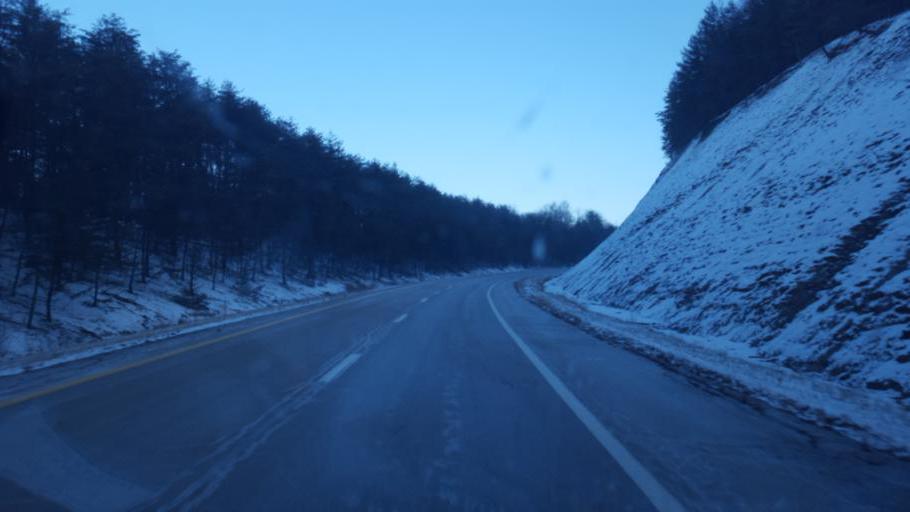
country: US
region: Ohio
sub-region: Adams County
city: Peebles
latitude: 39.0108
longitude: -83.2958
